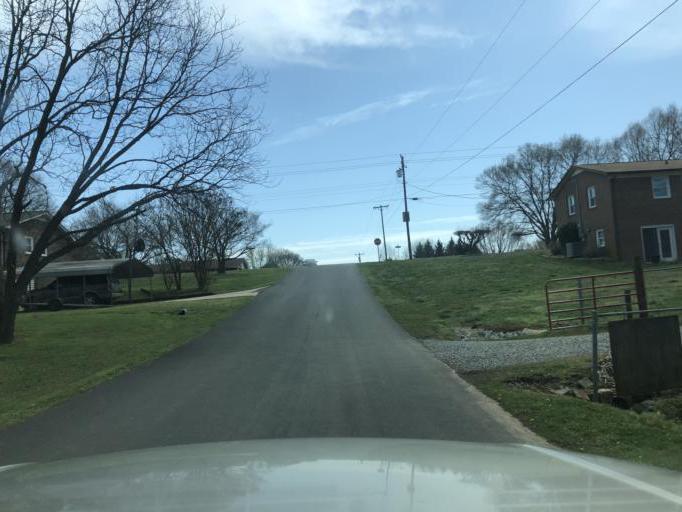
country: US
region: North Carolina
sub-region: Cleveland County
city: Shelby
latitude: 35.2487
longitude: -81.5343
